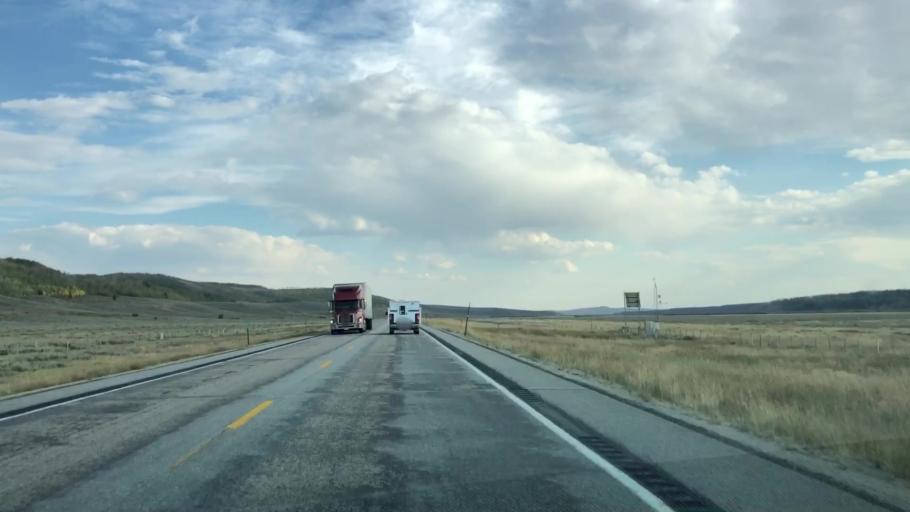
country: US
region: Wyoming
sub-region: Sublette County
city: Pinedale
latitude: 43.1064
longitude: -110.1718
